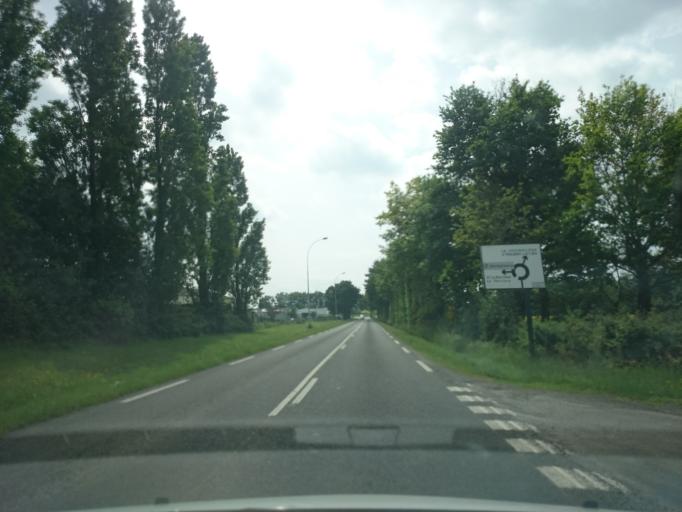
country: FR
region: Pays de la Loire
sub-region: Departement de la Loire-Atlantique
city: La Chevroliere
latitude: 47.1029
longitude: -1.5980
